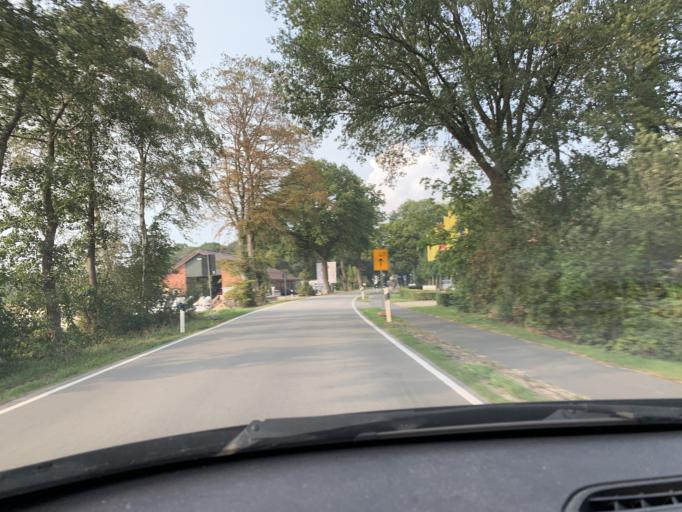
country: DE
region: Lower Saxony
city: Apen
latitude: 53.2111
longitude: 7.7955
